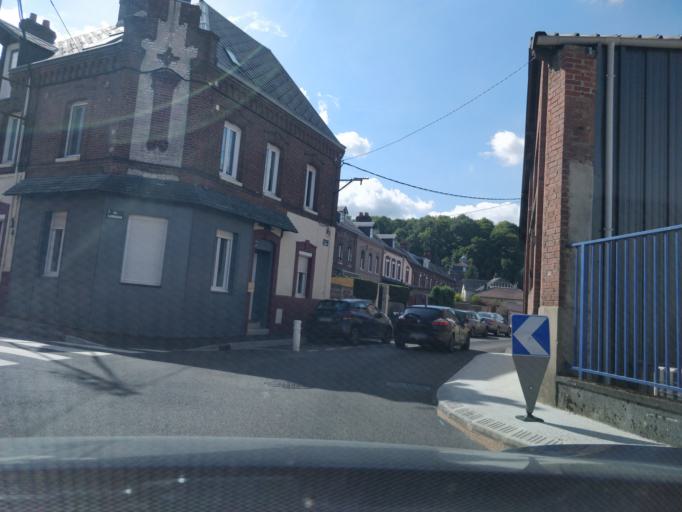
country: FR
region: Haute-Normandie
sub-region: Departement de la Seine-Maritime
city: Darnetal
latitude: 49.4366
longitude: 1.1490
